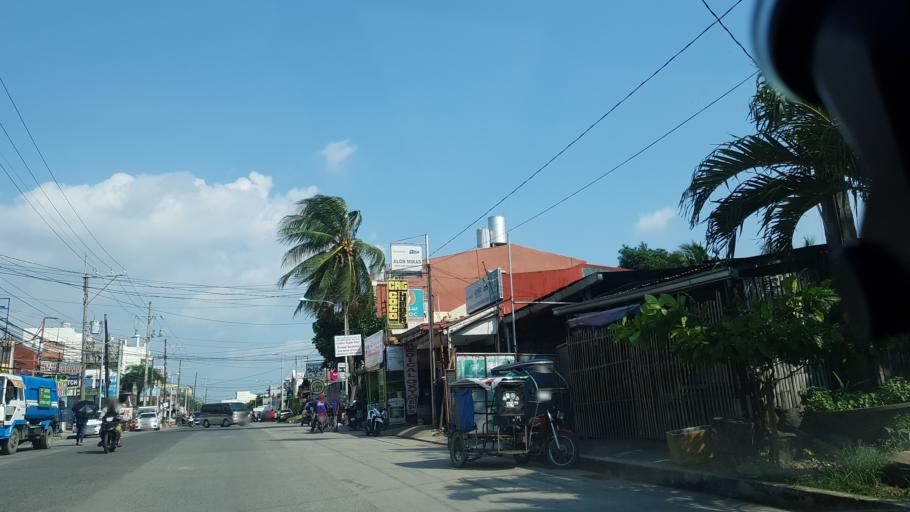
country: PH
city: Sambayanihan People's Village
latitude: 14.4895
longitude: 121.0193
